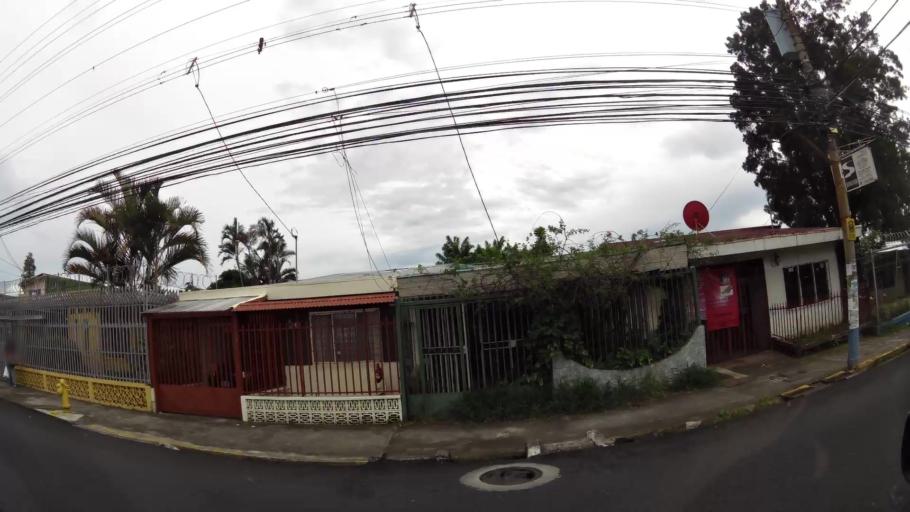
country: CR
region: San Jose
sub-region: Canton de Goicoechea
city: Guadalupe
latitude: 9.9495
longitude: -84.0552
